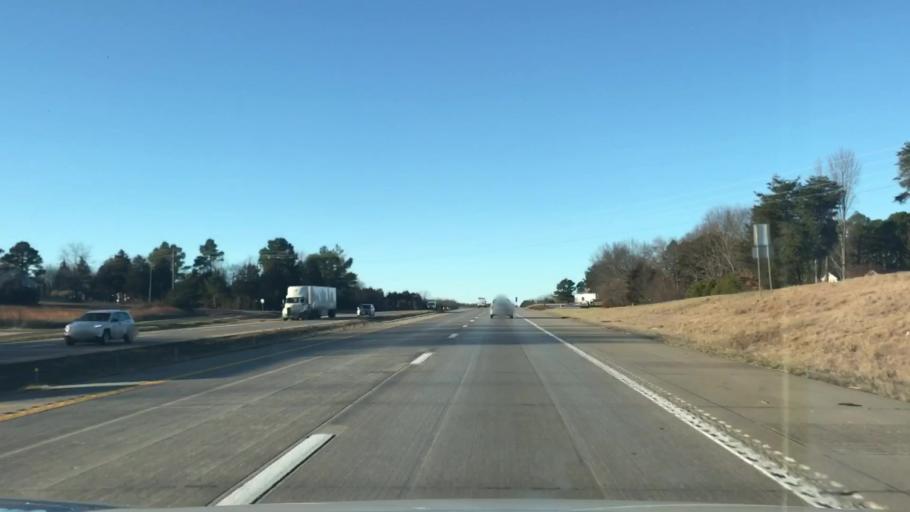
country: US
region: Missouri
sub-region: Crawford County
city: Bourbon
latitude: 38.1491
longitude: -91.2596
